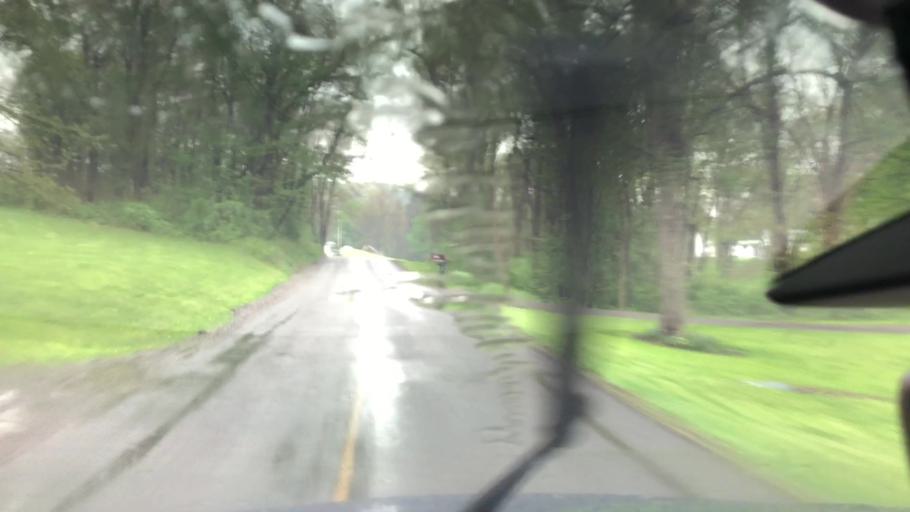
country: US
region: Pennsylvania
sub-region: Butler County
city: Saxonburg
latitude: 40.7418
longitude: -79.8562
